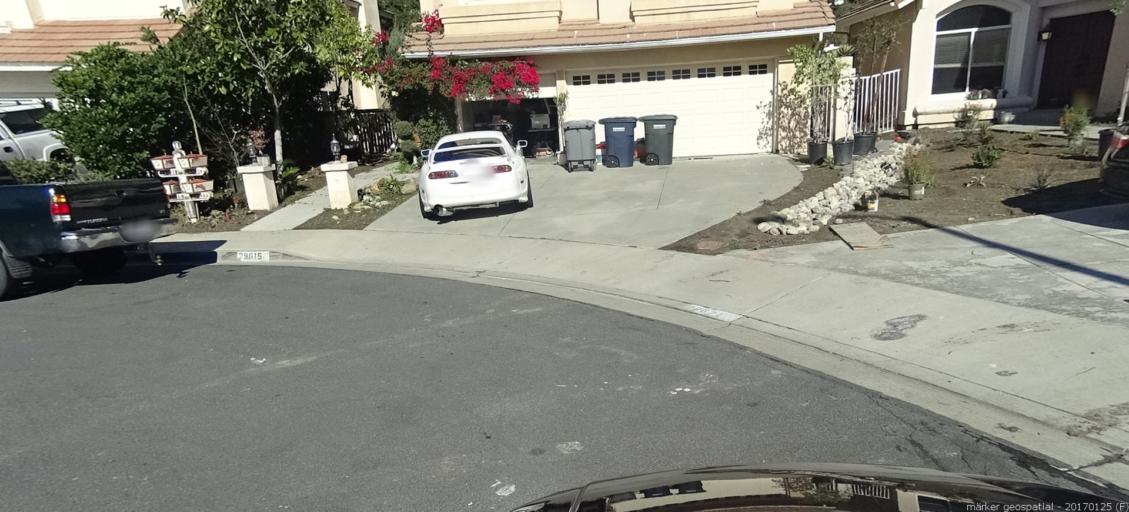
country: US
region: California
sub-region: Orange County
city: Portola Hills
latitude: 33.6843
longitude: -117.6315
